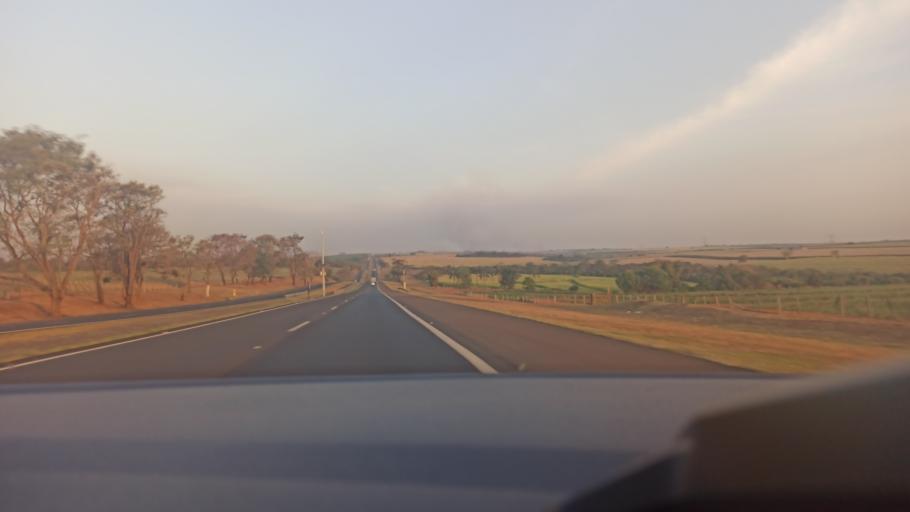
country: BR
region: Sao Paulo
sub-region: Taquaritinga
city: Taquaritinga
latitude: -21.4242
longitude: -48.6731
